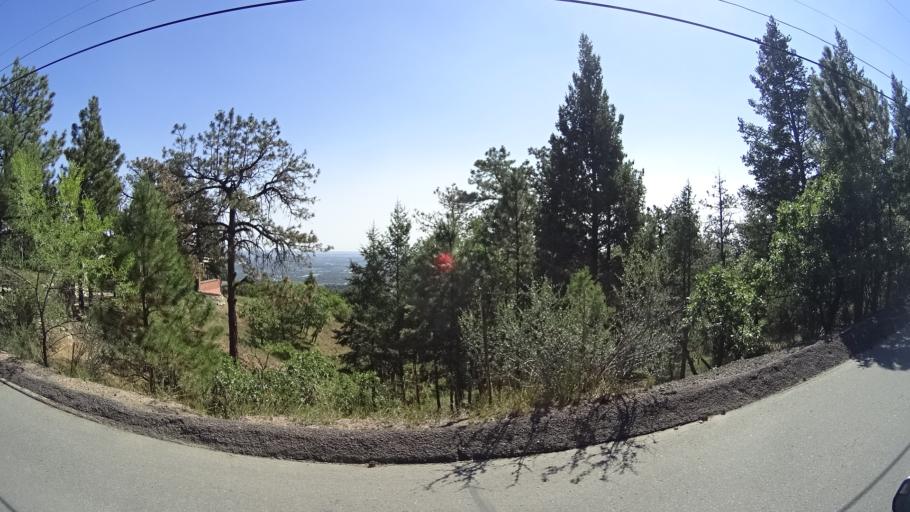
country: US
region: Colorado
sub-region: El Paso County
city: Colorado Springs
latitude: 38.8070
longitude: -104.8784
